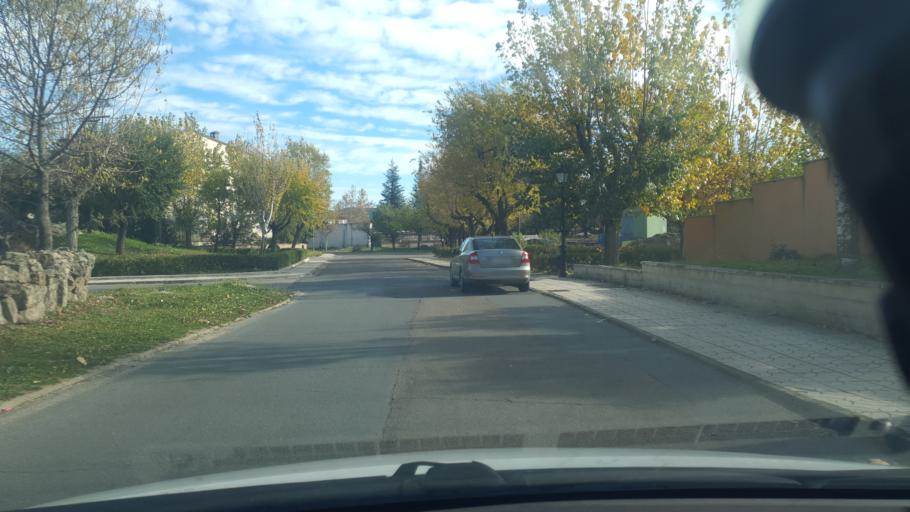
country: ES
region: Castille and Leon
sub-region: Provincia de Avila
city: Sotillo de la Adrada
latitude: 40.2916
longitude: -4.5927
